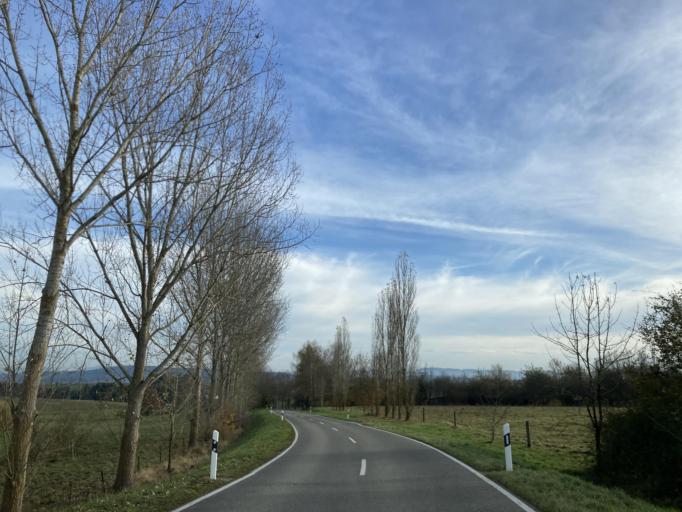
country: DE
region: Baden-Wuerttemberg
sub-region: Tuebingen Region
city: Hirrlingen
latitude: 48.4109
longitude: 8.8406
